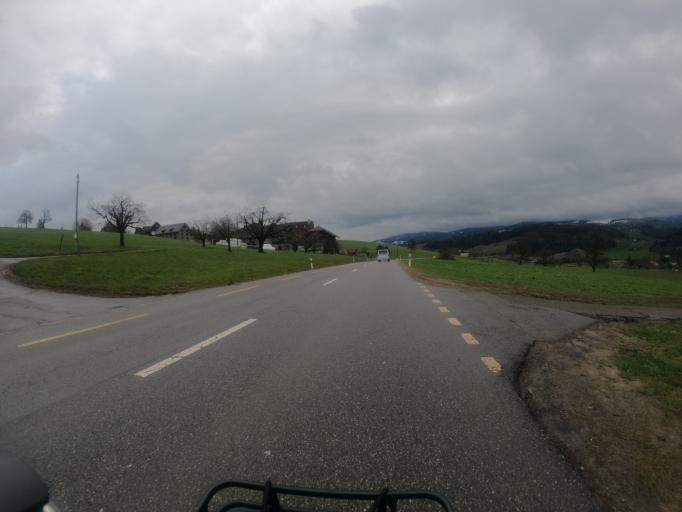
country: CH
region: Zurich
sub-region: Bezirk Affoltern
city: Hausen am Albis / Hausen (Dorf)
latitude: 47.2225
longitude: 8.5558
